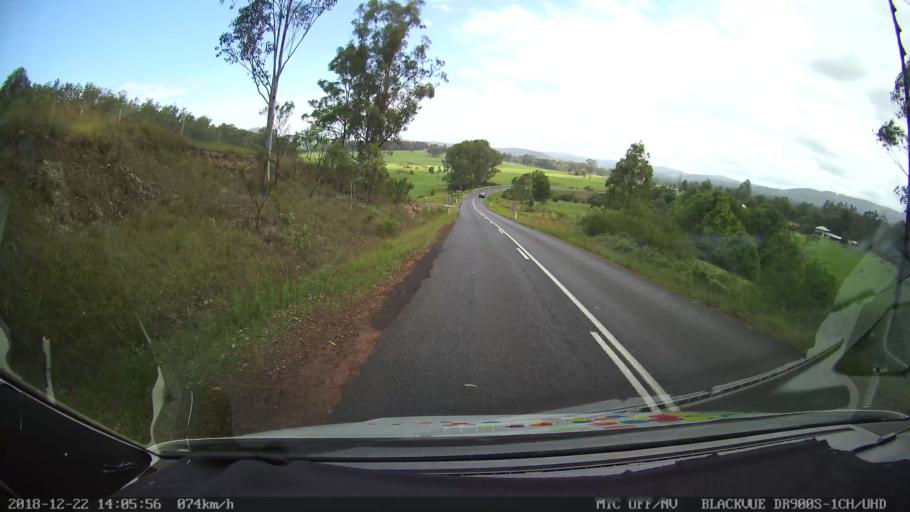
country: AU
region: New South Wales
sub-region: Clarence Valley
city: Coutts Crossing
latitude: -29.9503
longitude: 152.7286
